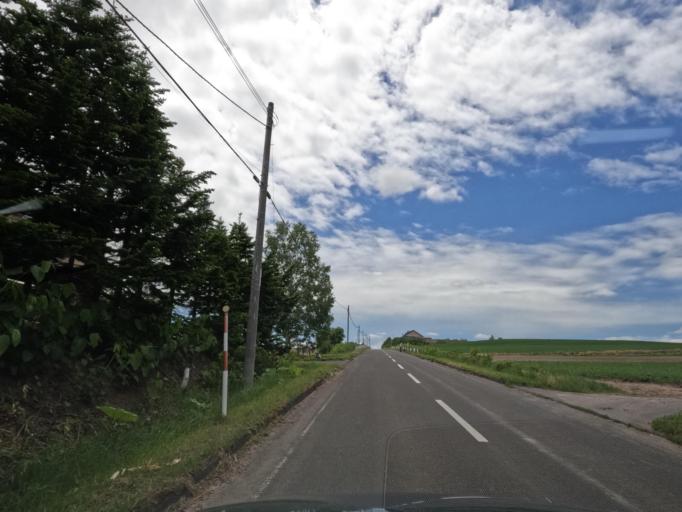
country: JP
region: Hokkaido
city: Shimo-furano
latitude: 43.5288
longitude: 142.4378
